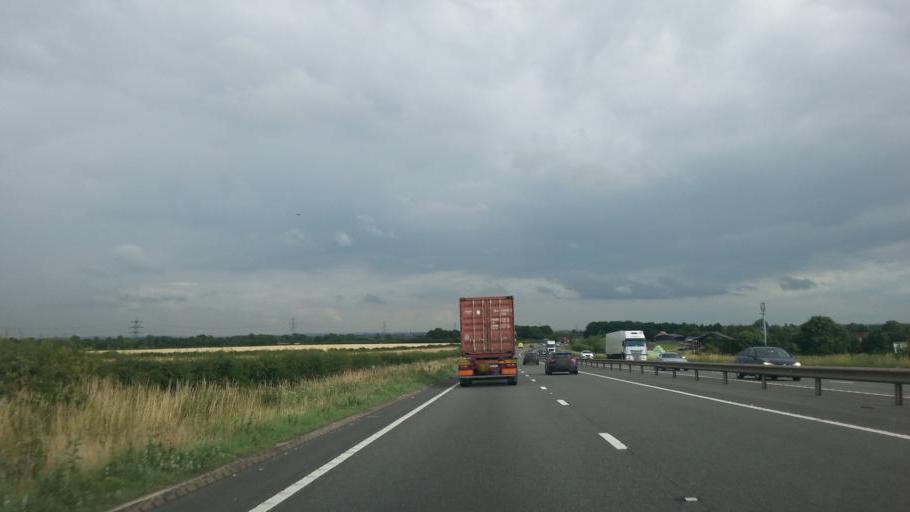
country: GB
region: England
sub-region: Nottinghamshire
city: Newark on Trent
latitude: 53.0695
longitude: -0.7668
